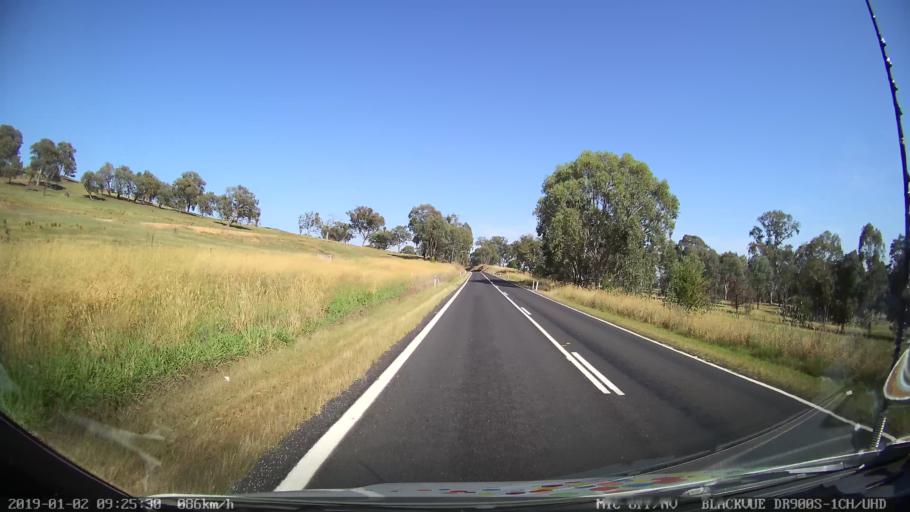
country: AU
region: New South Wales
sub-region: Tumut Shire
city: Tumut
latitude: -35.3658
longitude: 148.2853
